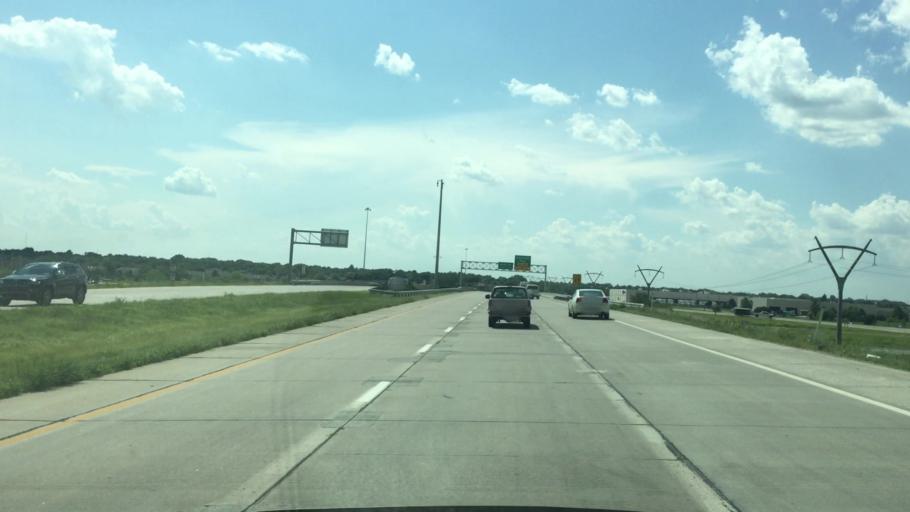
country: US
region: Kansas
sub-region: Sedgwick County
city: Bellaire
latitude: 37.7299
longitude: -97.2060
